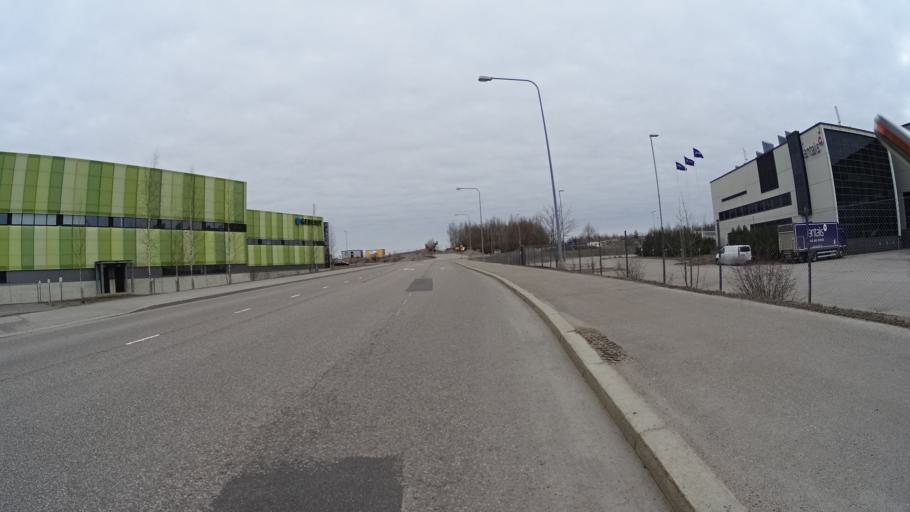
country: FI
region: Uusimaa
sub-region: Helsinki
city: Vantaa
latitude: 60.3024
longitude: 24.9123
